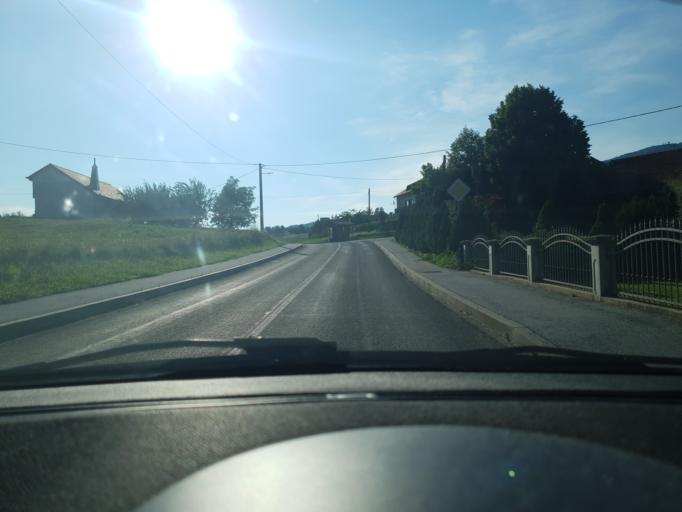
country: HR
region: Krapinsko-Zagorska
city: Radoboj
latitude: 46.1628
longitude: 15.9342
